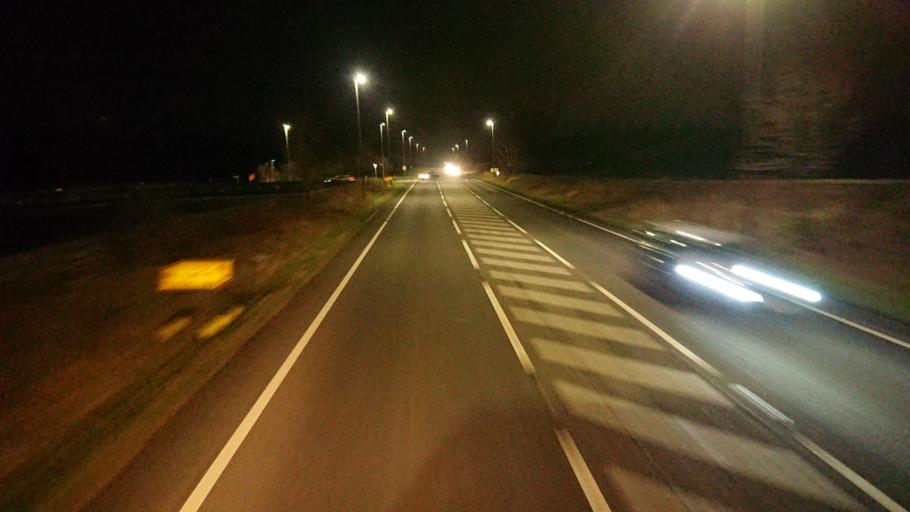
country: GB
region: England
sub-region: Cumbria
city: Kendal
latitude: 54.3690
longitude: -2.8080
